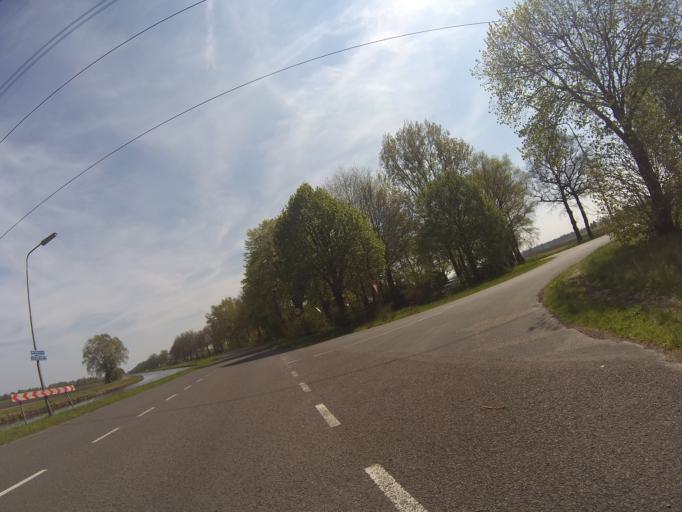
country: NL
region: Drenthe
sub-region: Gemeente Coevorden
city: Sleen
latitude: 52.7232
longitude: 6.8119
